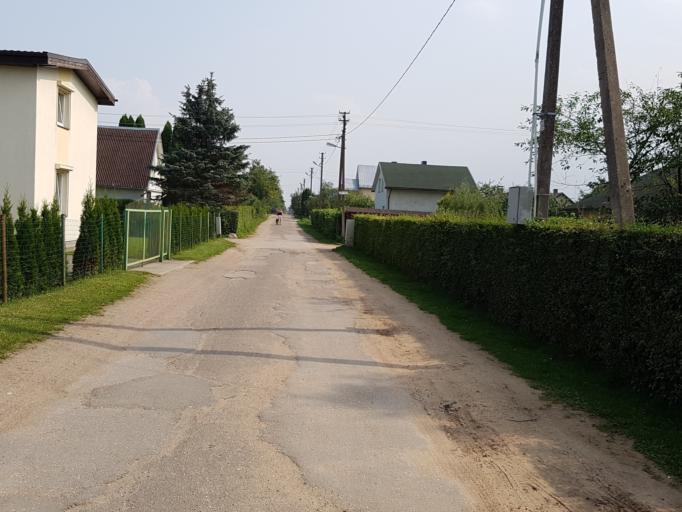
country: LT
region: Vilnius County
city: Rasos
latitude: 54.7931
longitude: 25.3636
